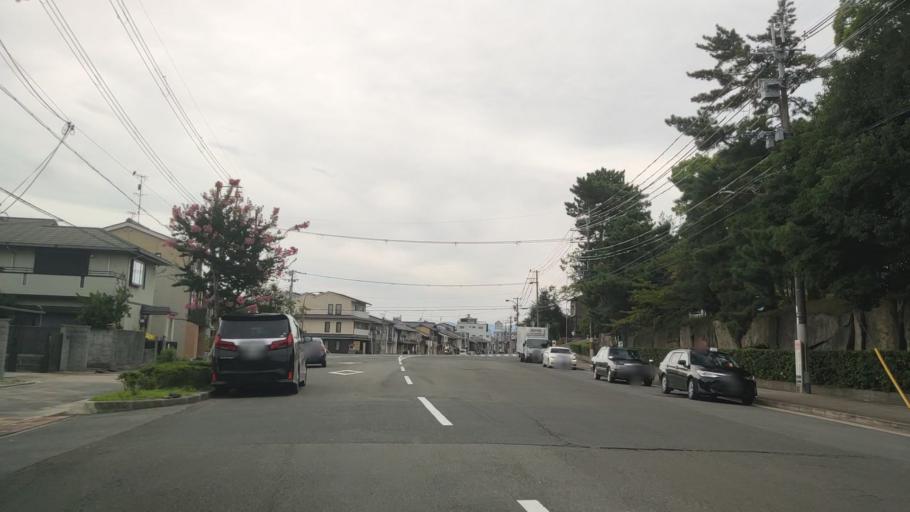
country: JP
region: Kyoto
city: Kyoto
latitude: 34.9909
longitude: 135.7712
